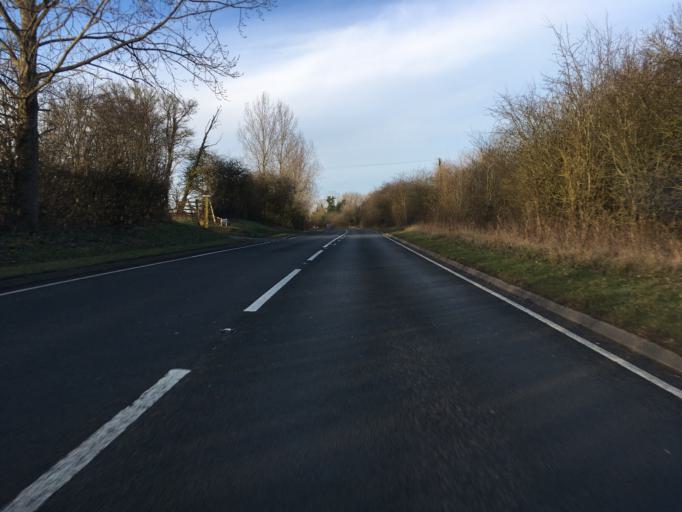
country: GB
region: England
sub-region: Warwickshire
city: Stratford-upon-Avon
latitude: 52.2280
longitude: -1.7398
